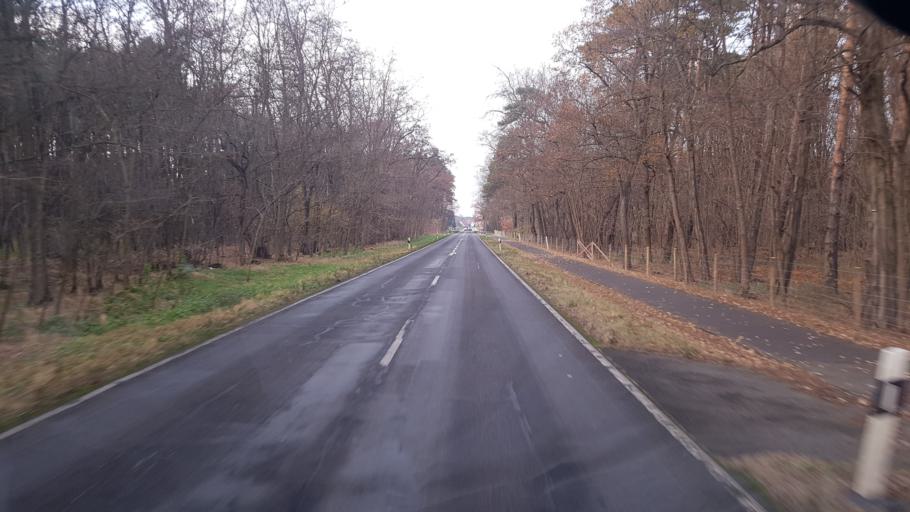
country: DE
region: Brandenburg
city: Ziltendorf
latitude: 52.1982
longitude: 14.6364
